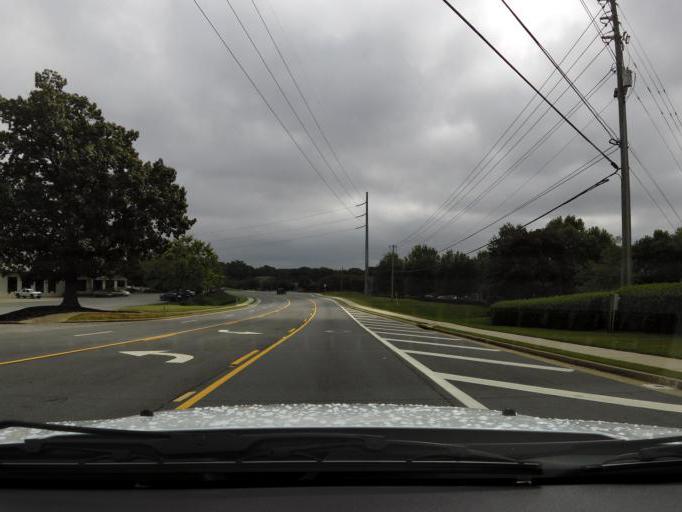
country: US
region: Georgia
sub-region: Cobb County
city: Kennesaw
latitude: 34.0496
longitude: -84.5908
